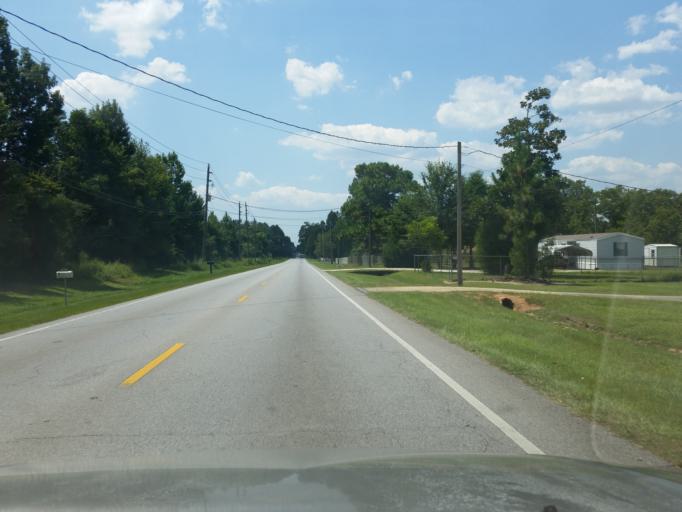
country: US
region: Florida
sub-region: Escambia County
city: Cantonment
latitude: 30.6414
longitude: -87.3180
